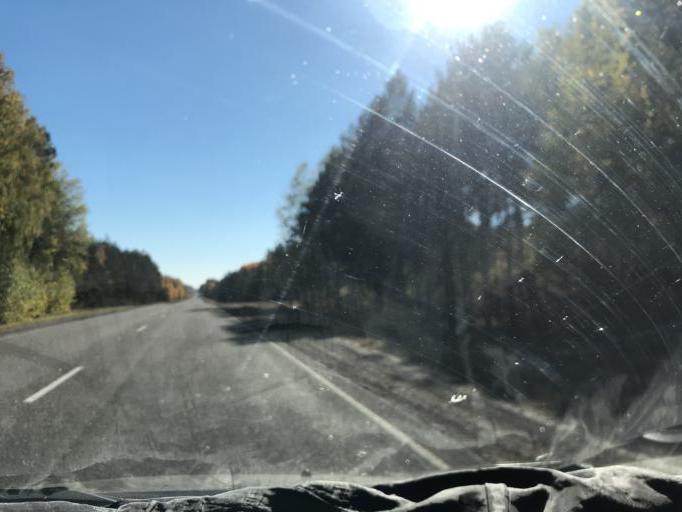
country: BY
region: Gomel
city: Kalinkavichy
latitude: 52.4246
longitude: 29.2875
